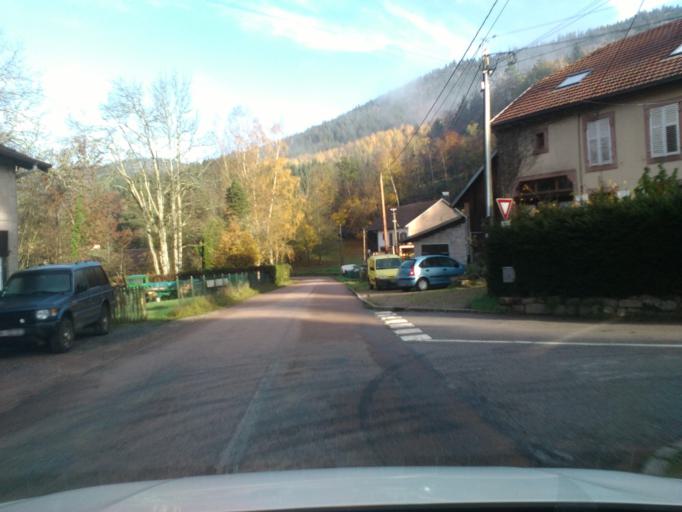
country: FR
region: Lorraine
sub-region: Departement des Vosges
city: Senones
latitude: 48.4222
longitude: 7.0384
